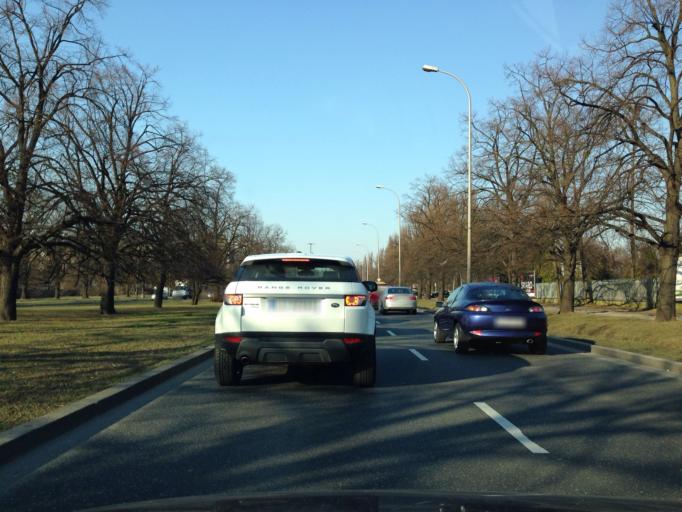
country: PL
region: Masovian Voivodeship
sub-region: Warszawa
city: Ochota
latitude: 52.2083
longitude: 20.9874
